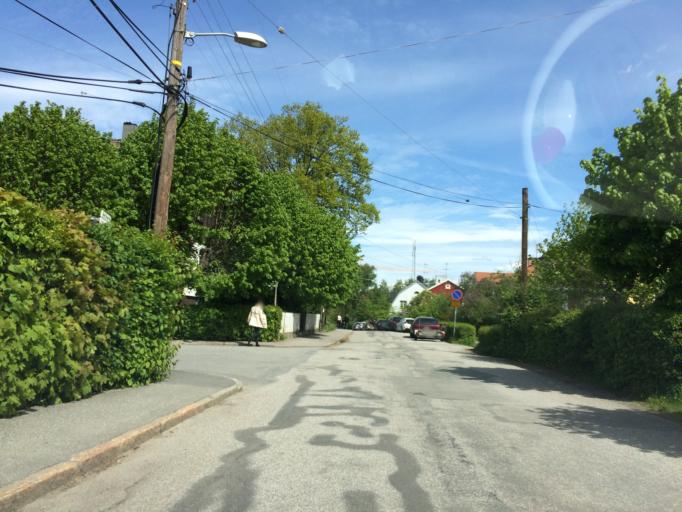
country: SE
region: Stockholm
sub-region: Huddinge Kommun
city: Huddinge
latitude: 59.2755
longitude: 18.0041
